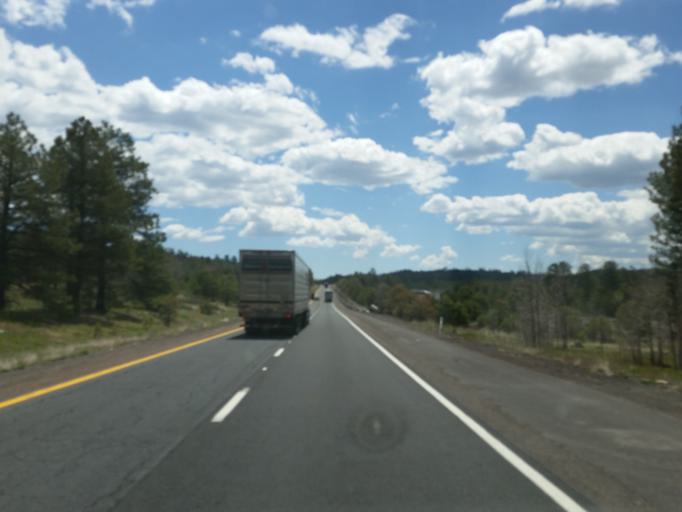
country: US
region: Arizona
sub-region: Coconino County
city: Parks
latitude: 35.2557
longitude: -111.9223
